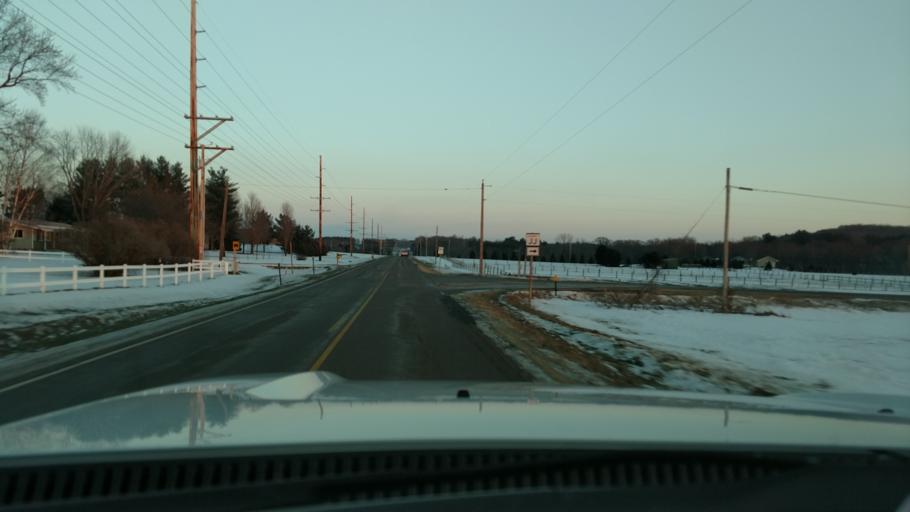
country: US
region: Wisconsin
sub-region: Saint Croix County
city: Roberts
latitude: 44.9131
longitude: -92.5436
